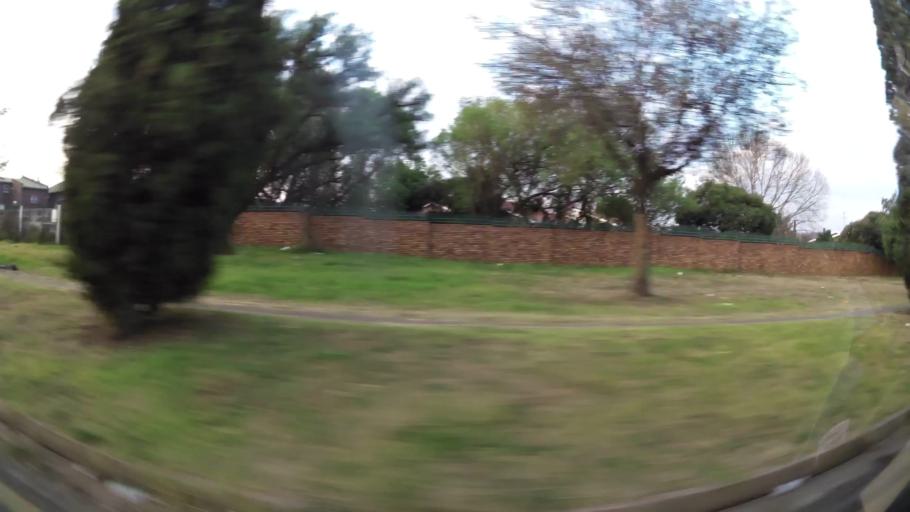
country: ZA
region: Gauteng
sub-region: Ekurhuleni Metropolitan Municipality
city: Benoni
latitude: -26.1679
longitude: 28.3100
